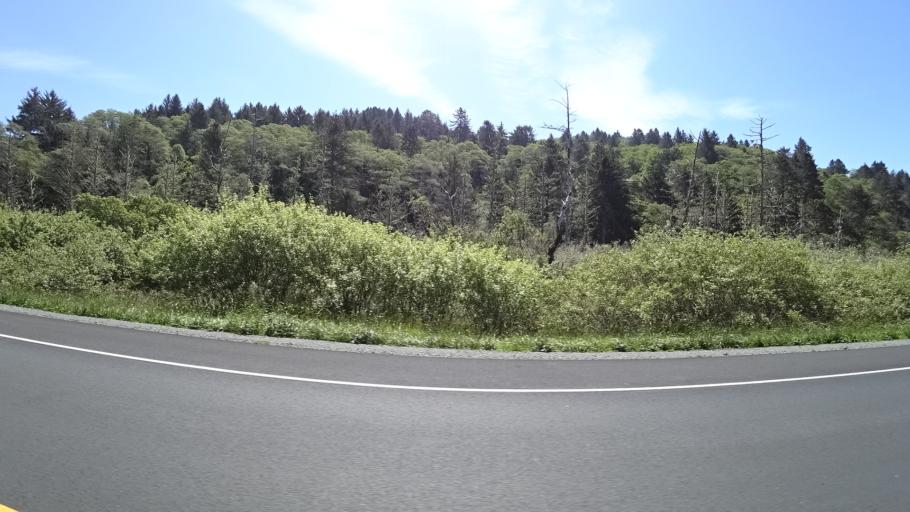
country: US
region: California
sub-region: Humboldt County
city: Westhaven-Moonstone
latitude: 41.2851
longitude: -124.0884
